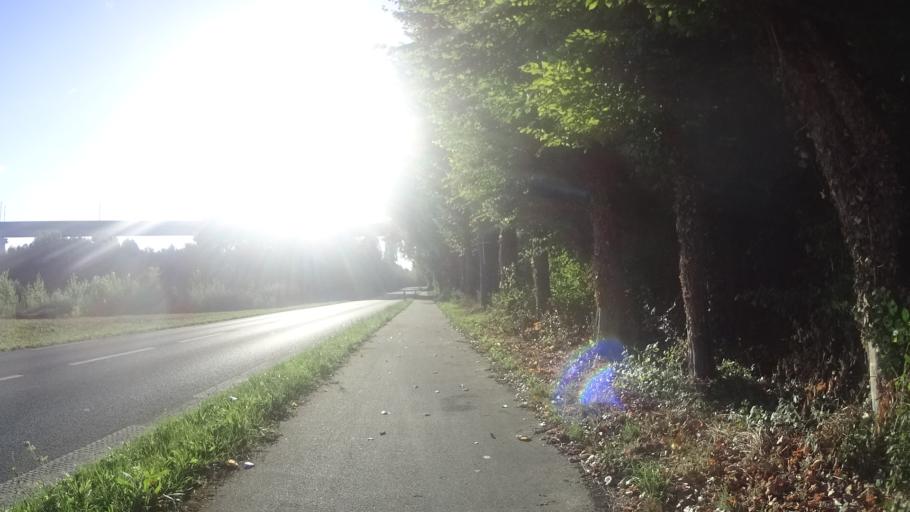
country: FR
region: Picardie
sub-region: Departement de l'Oise
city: Verberie
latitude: 49.3080
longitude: 2.7099
